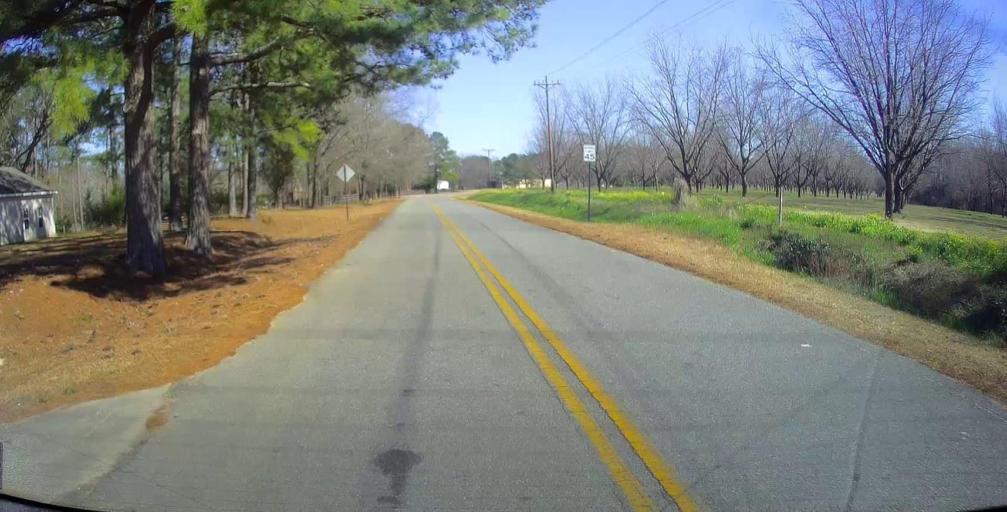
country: US
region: Georgia
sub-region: Peach County
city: Fort Valley
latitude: 32.6325
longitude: -83.8537
